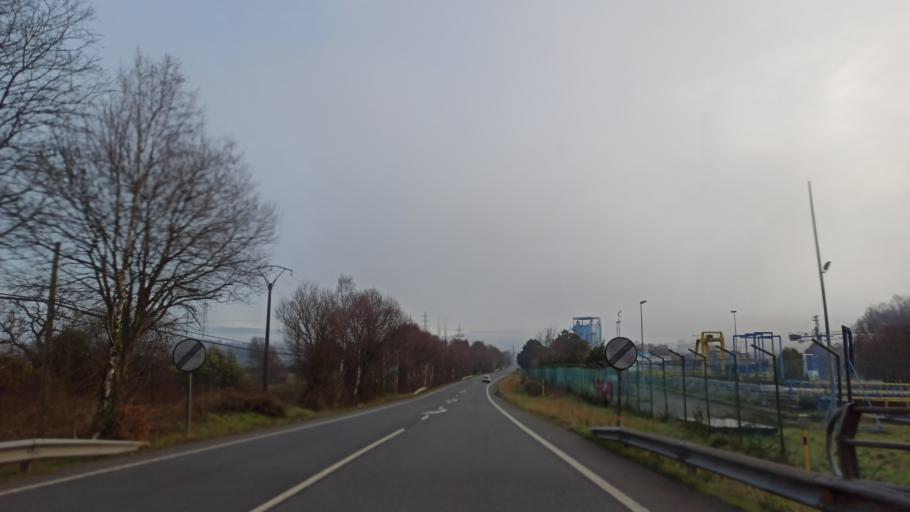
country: ES
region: Galicia
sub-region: Provincia da Coruna
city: As Pontes de Garcia Rodriguez
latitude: 43.4402
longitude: -7.8744
